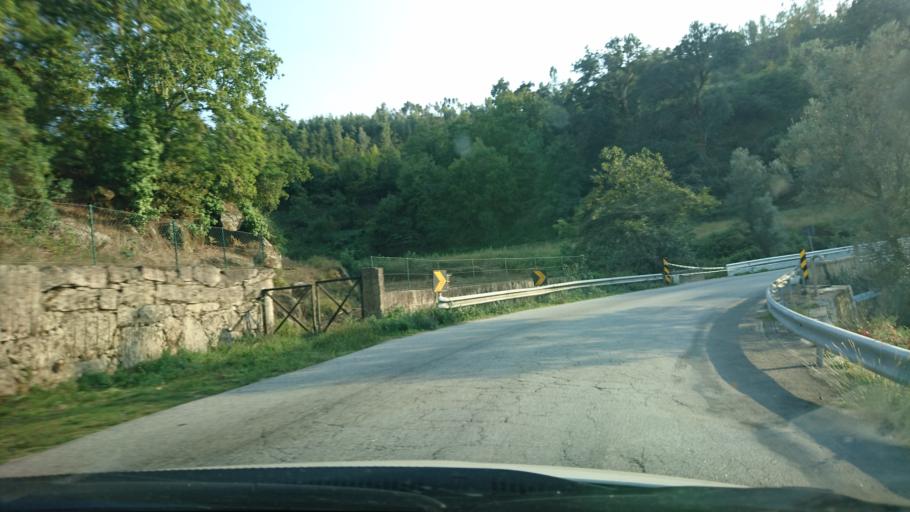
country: PT
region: Vila Real
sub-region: Mondim de Basto
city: Mondim de Basto
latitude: 41.4165
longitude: -7.9372
